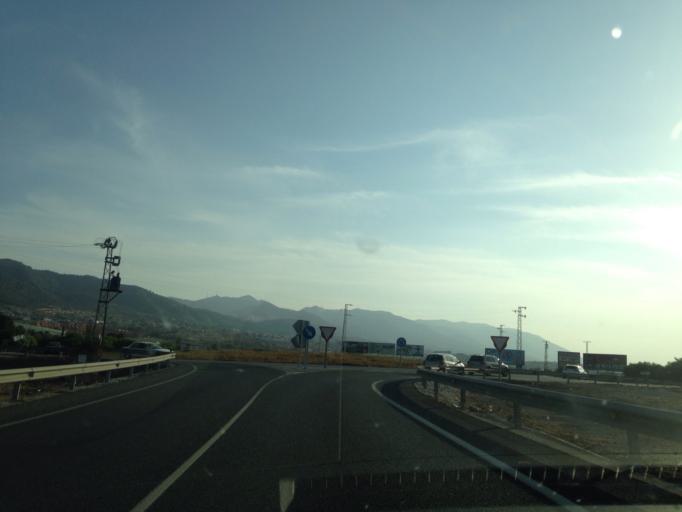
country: ES
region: Andalusia
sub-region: Provincia de Malaga
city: Alhaurin de la Torre
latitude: 36.6761
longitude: -4.5329
